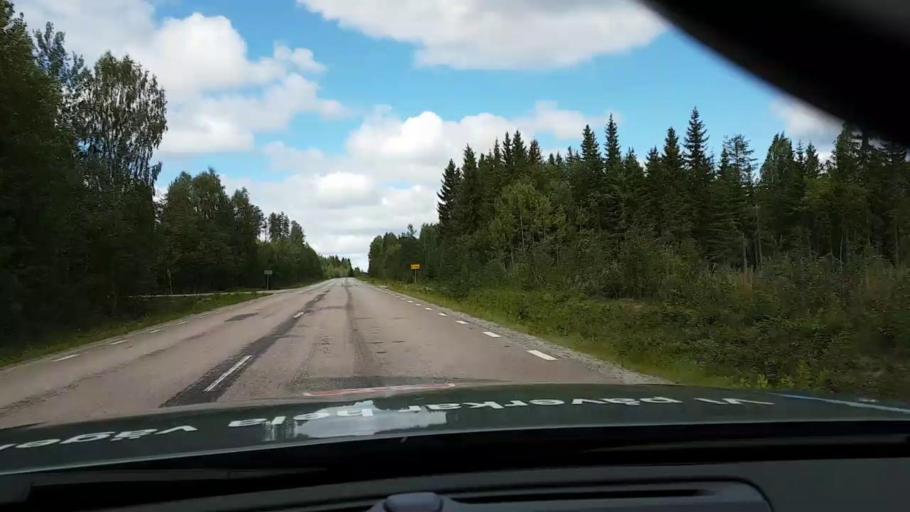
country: SE
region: Vaesternorrland
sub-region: OErnskoeldsviks Kommun
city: Bredbyn
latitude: 63.4698
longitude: 18.1007
